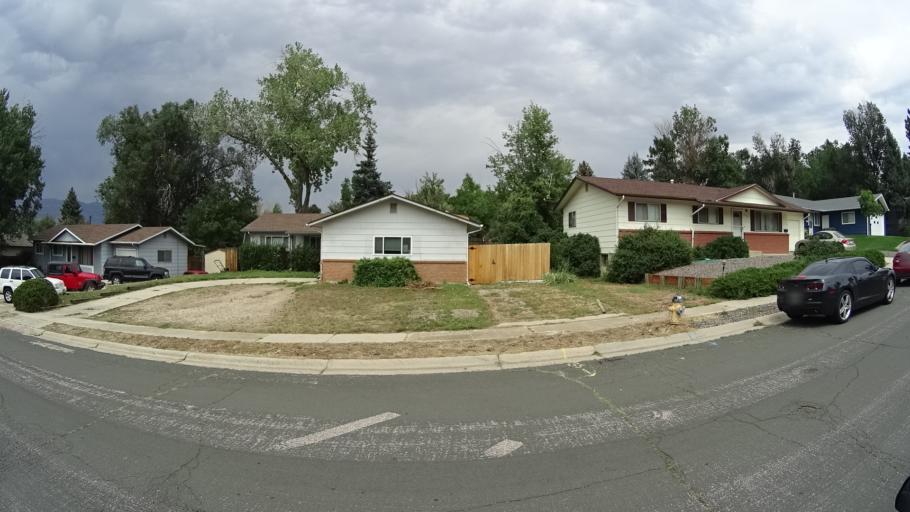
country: US
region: Colorado
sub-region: El Paso County
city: Colorado Springs
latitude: 38.8935
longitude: -104.8114
